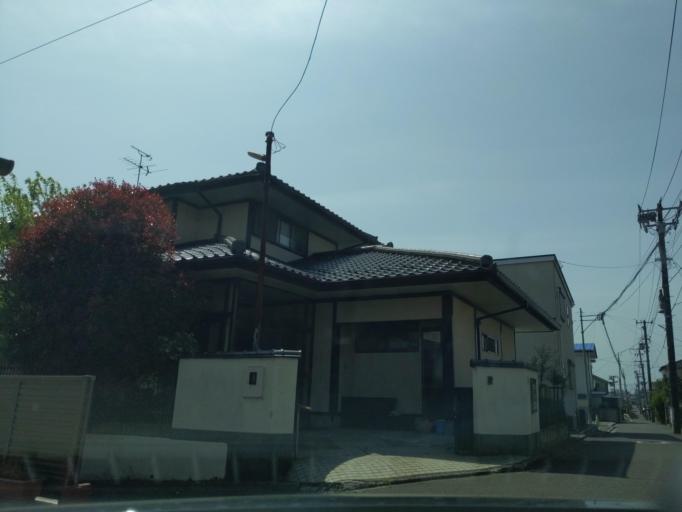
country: JP
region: Fukushima
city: Koriyama
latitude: 37.3758
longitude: 140.3698
